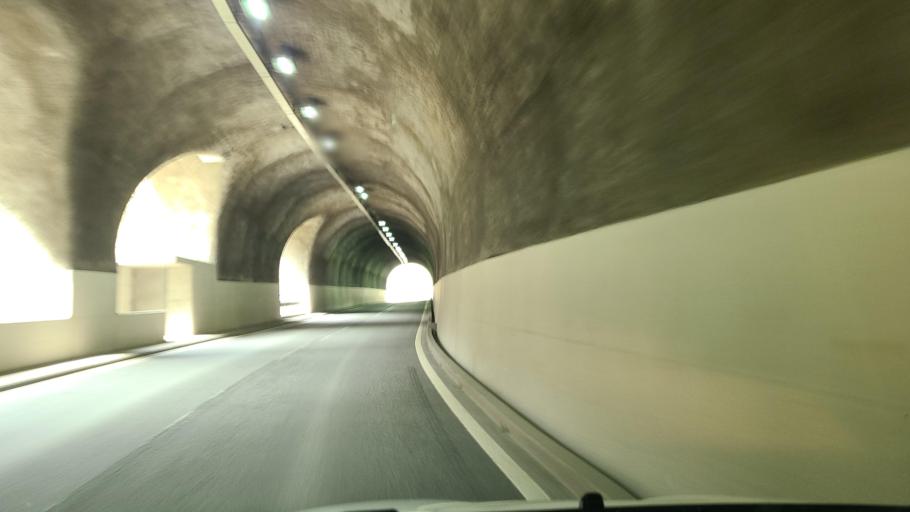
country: CH
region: Ticino
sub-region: Leventina District
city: Airolo
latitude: 46.5247
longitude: 8.6281
